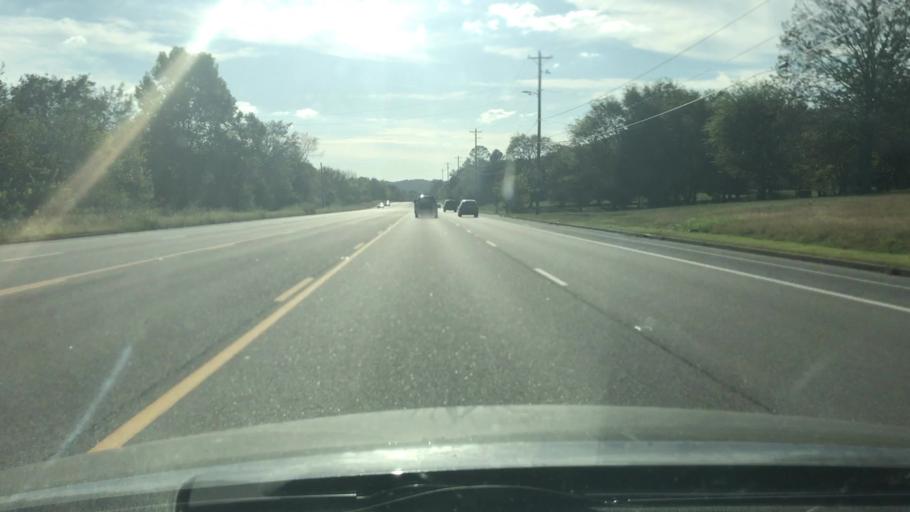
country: US
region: Tennessee
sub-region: Davidson County
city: Belle Meade
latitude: 36.2102
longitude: -86.9286
